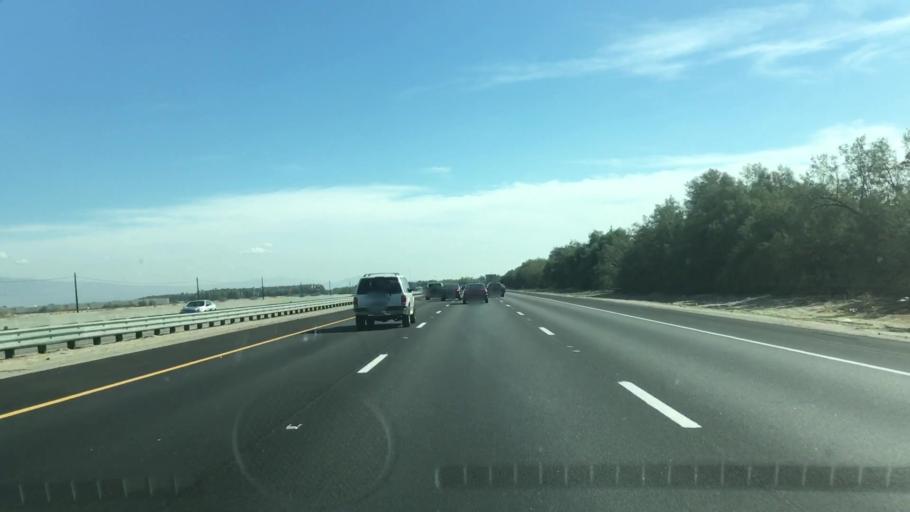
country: US
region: California
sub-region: Riverside County
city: Bermuda Dunes
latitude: 33.7698
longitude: -116.3275
